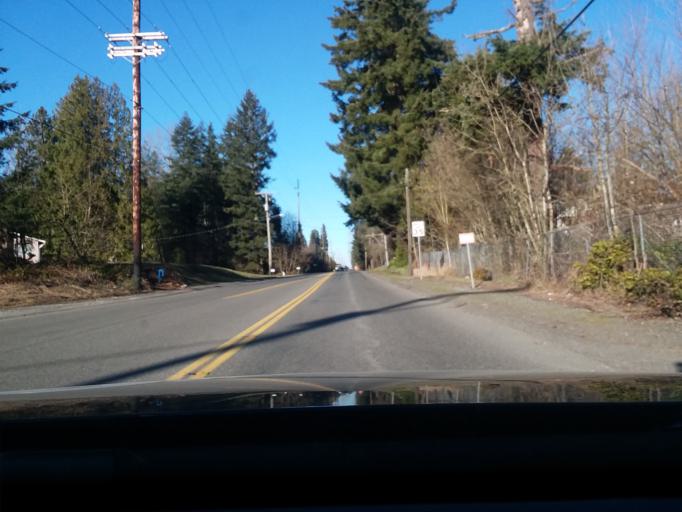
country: US
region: Washington
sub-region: Pierce County
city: Summit
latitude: 47.1400
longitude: -122.3582
